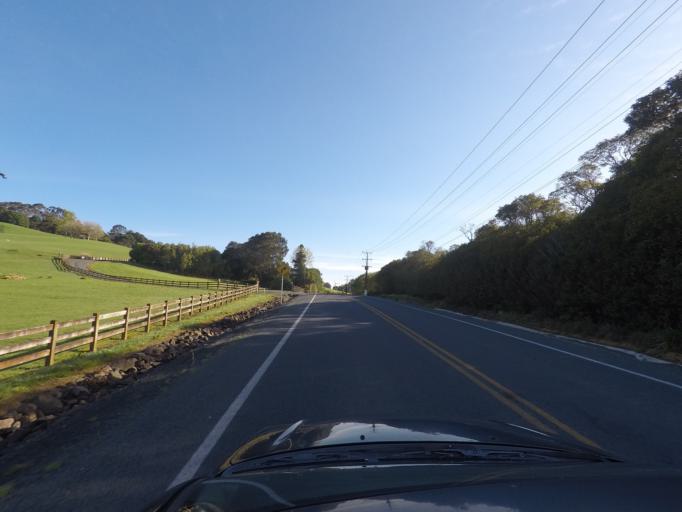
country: NZ
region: Auckland
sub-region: Auckland
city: Red Hill
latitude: -36.9942
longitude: 174.9845
